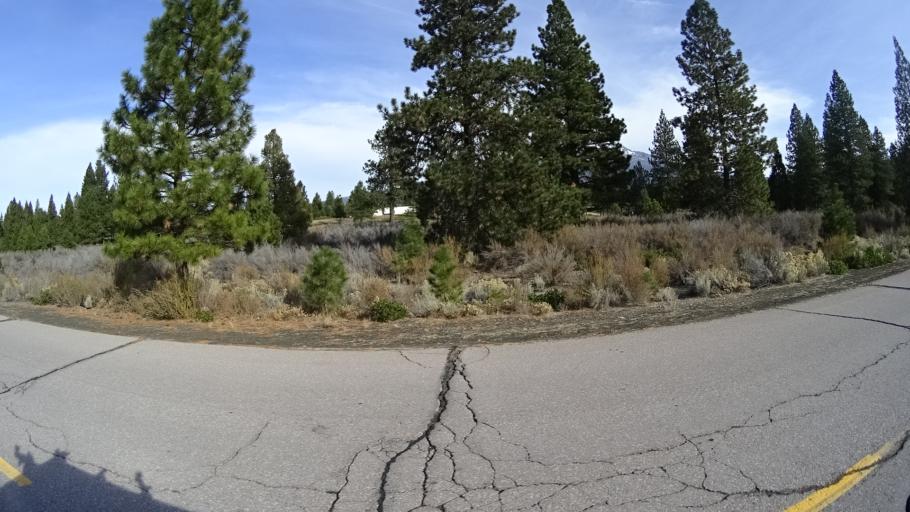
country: US
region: California
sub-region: Siskiyou County
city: Weed
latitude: 41.3960
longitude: -122.3828
